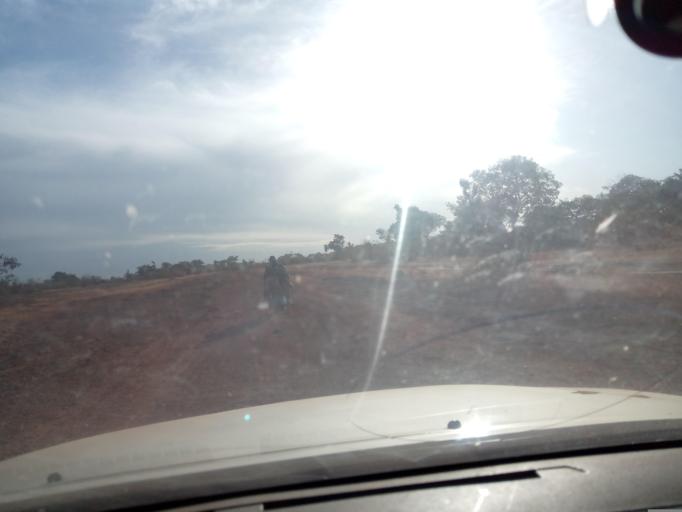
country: ML
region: Sikasso
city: Sikasso
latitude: 11.4101
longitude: -5.5705
